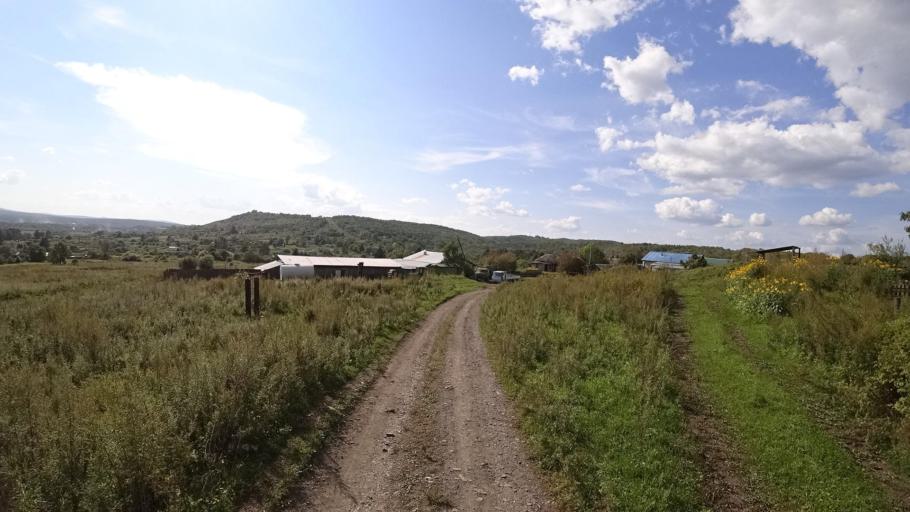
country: RU
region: Jewish Autonomous Oblast
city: Birakan
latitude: 49.0086
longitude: 131.7442
